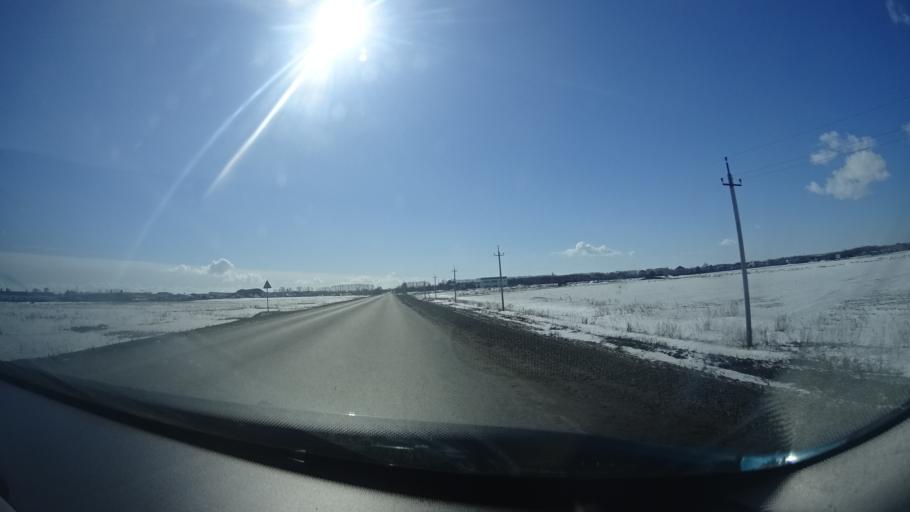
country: RU
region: Bashkortostan
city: Ufa
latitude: 54.6233
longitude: 55.8932
